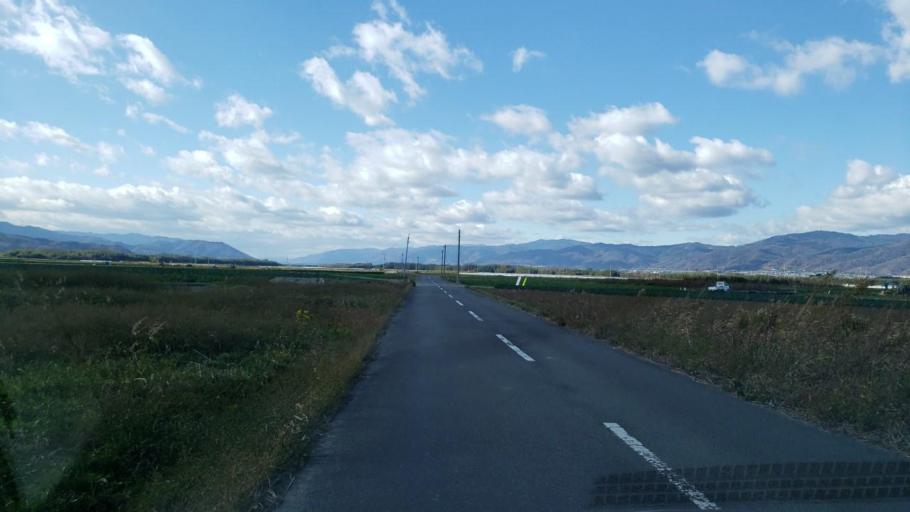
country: JP
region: Tokushima
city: Kamojimacho-jogejima
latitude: 34.0699
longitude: 134.3099
